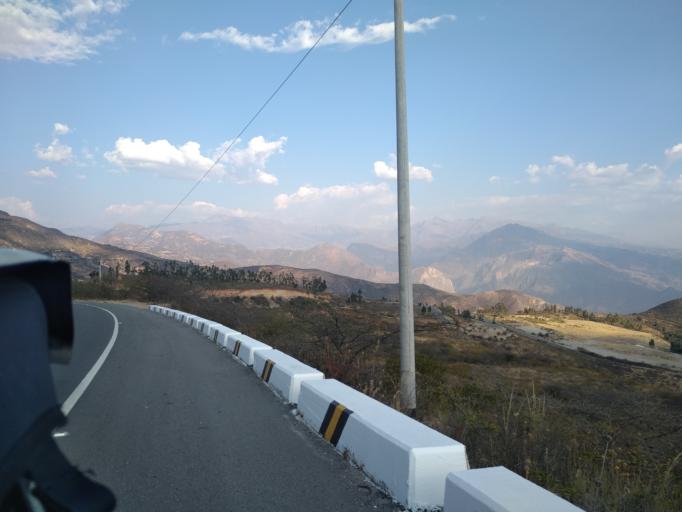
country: PE
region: Cajamarca
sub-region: San Marcos
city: La Grama
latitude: -7.4053
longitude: -78.1226
